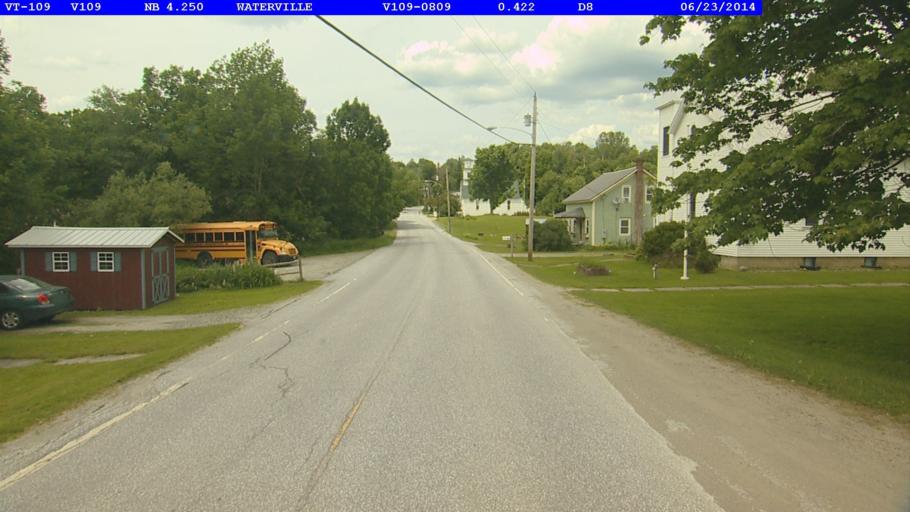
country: US
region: Vermont
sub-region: Lamoille County
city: Johnson
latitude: 44.6886
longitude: -72.7692
